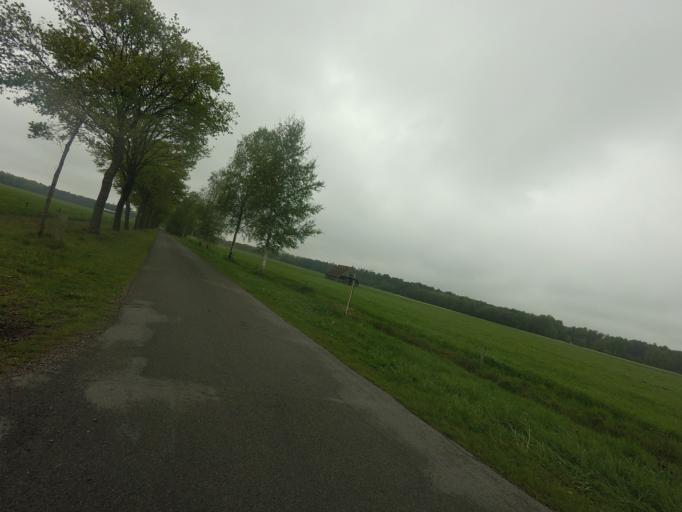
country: DE
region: North Rhine-Westphalia
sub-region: Regierungsbezirk Munster
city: Vreden
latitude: 52.1262
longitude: 6.8298
